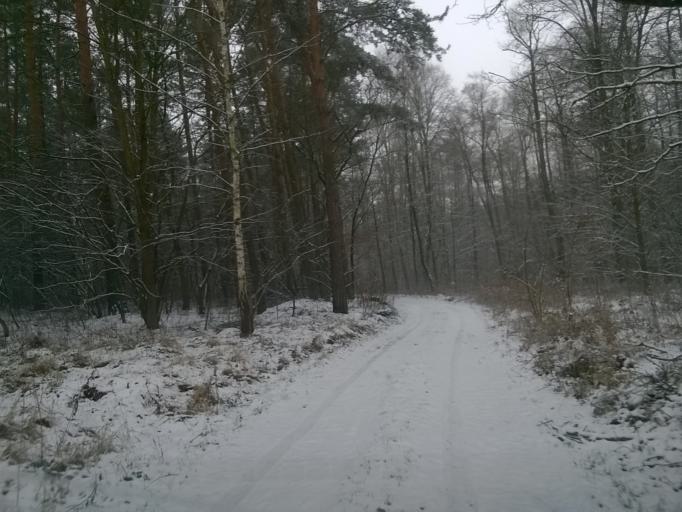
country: PL
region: Kujawsko-Pomorskie
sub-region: Powiat swiecki
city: Swiecie
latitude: 53.4222
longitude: 18.3882
